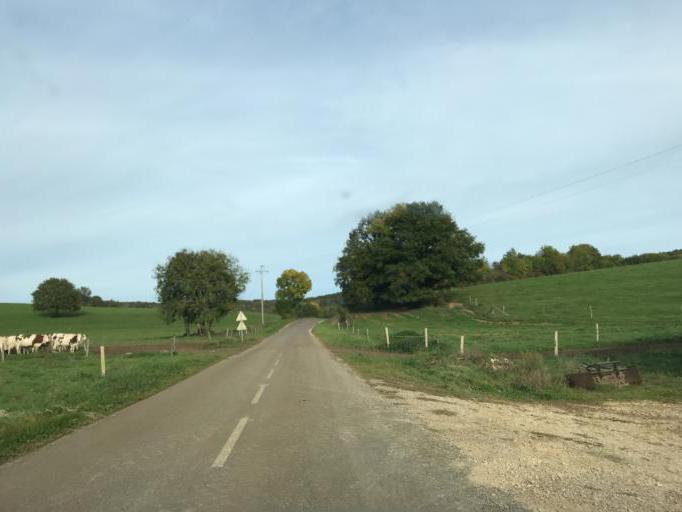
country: FR
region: Bourgogne
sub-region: Departement de Saone-et-Loire
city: Cuiseaux
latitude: 46.4925
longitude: 5.4911
